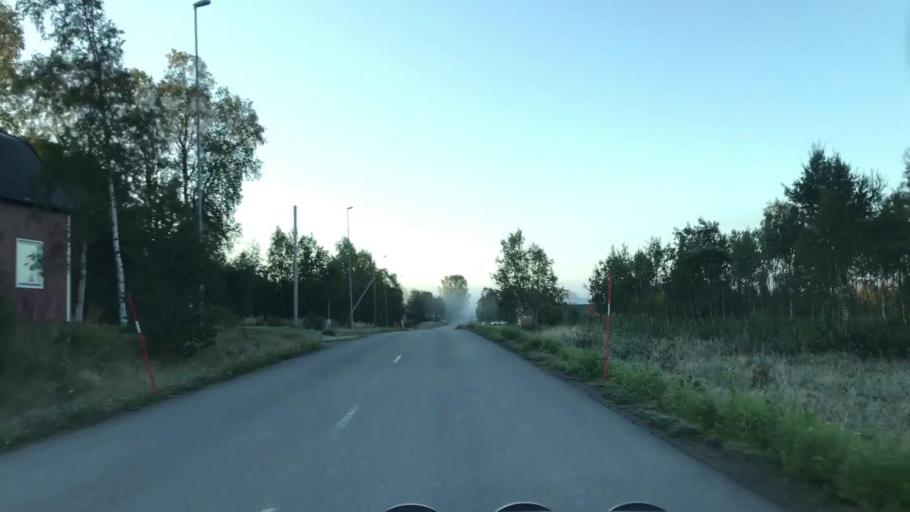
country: SE
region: Norrbotten
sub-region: Gallivare Kommun
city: Malmberget
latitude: 67.6499
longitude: 21.0445
